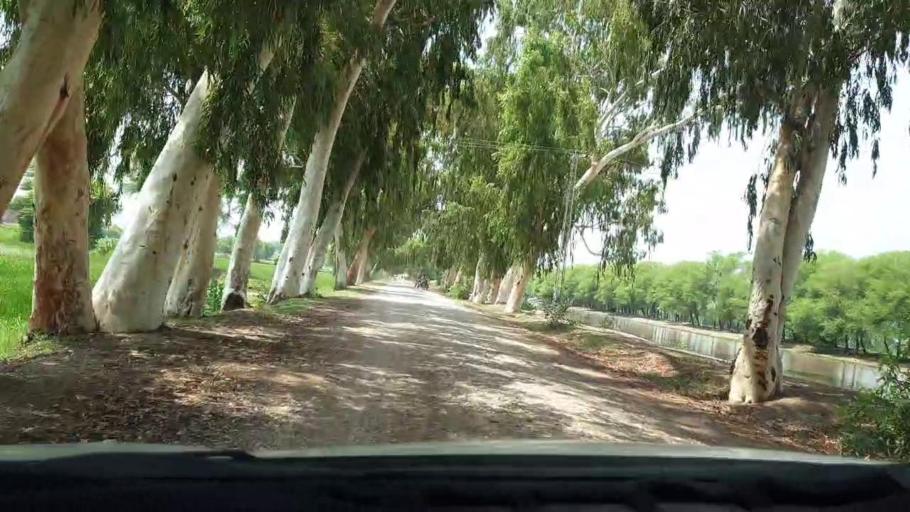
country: PK
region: Sindh
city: New Badah
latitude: 27.2994
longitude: 68.0893
